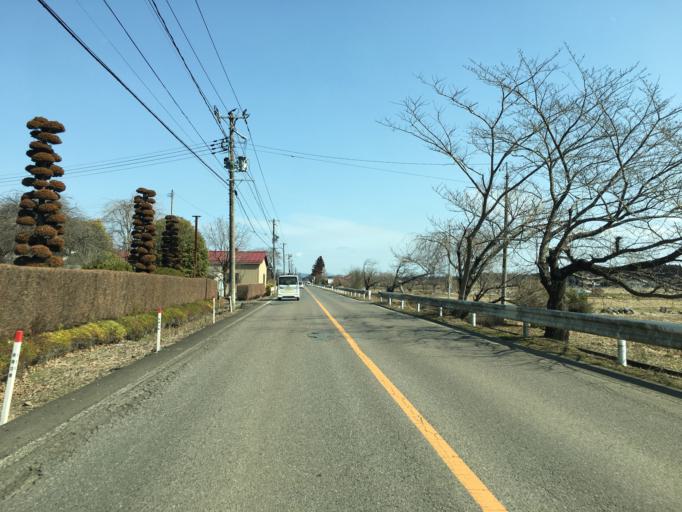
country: JP
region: Fukushima
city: Ishikawa
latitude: 37.1378
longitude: 140.3339
